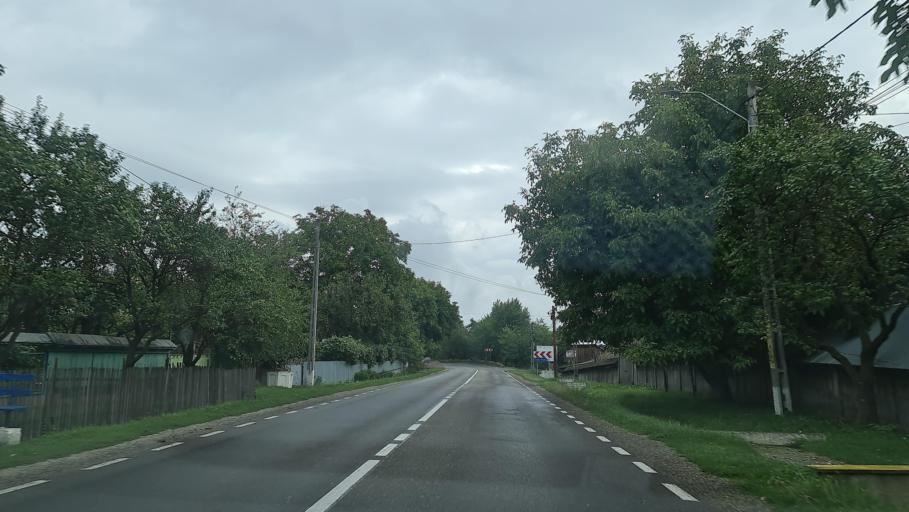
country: RO
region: Neamt
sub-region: Comuna Borlesti
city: Borlesti
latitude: 46.7727
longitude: 26.4926
